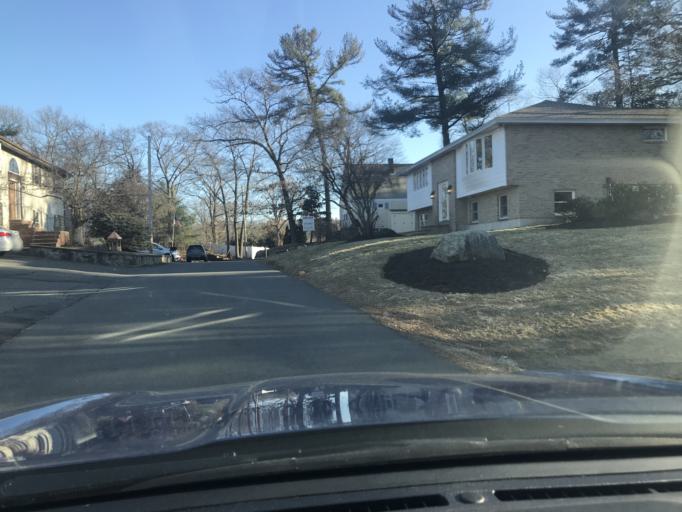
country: US
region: Massachusetts
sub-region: Essex County
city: Saugus
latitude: 42.4921
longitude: -71.0142
